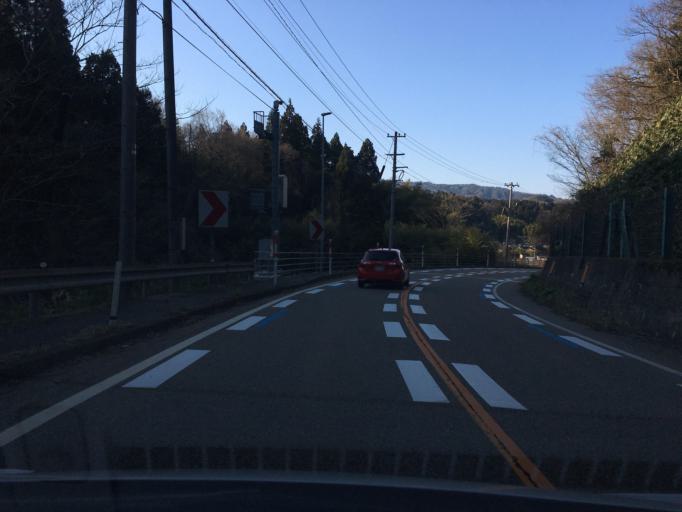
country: JP
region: Toyama
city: Himi
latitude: 36.9273
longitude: 137.0258
